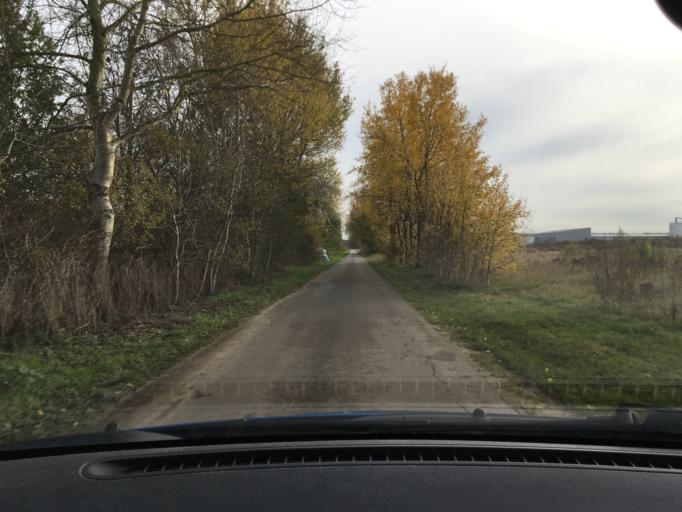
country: DE
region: Lower Saxony
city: Wittorf
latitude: 53.3174
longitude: 10.3745
